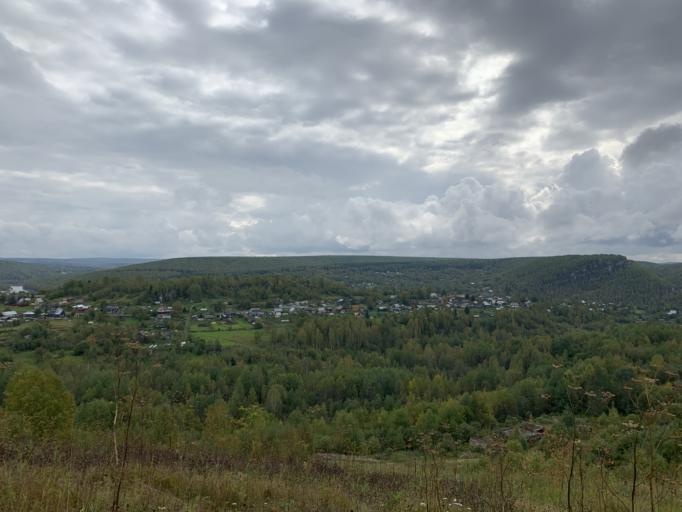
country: RU
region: Perm
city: Gubakha
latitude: 58.8724
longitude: 57.6044
